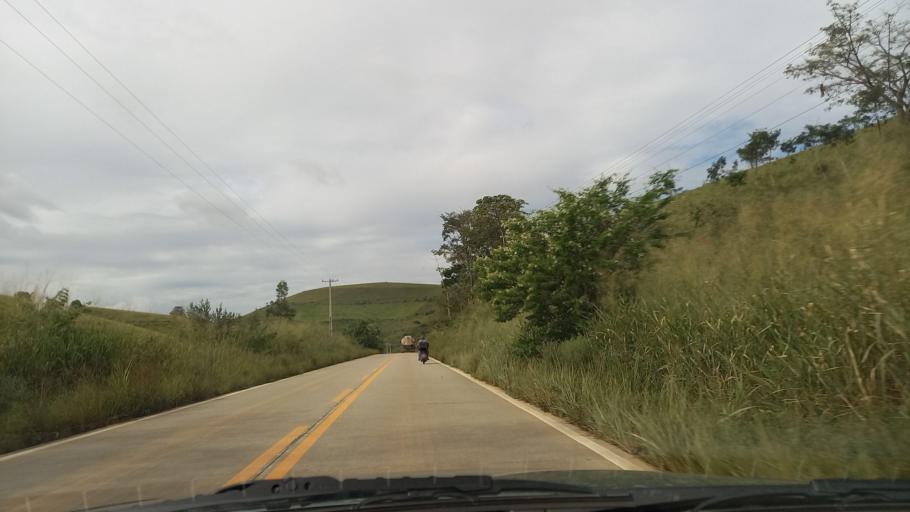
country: BR
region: Pernambuco
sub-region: Maraial
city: Maraial
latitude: -8.7508
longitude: -35.8360
